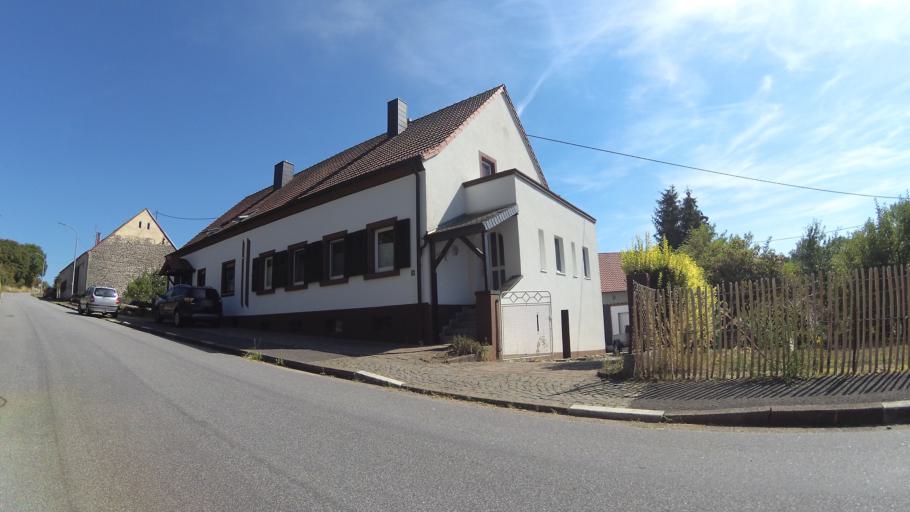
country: FR
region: Lorraine
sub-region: Departement de la Moselle
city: Petit-Rederching
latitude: 49.1425
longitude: 7.2889
